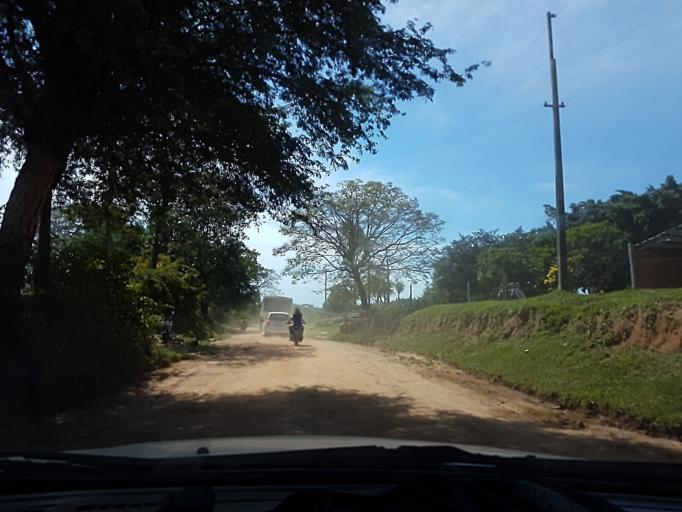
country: PY
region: Cordillera
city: Arroyos y Esteros
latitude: -24.9883
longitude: -57.2110
